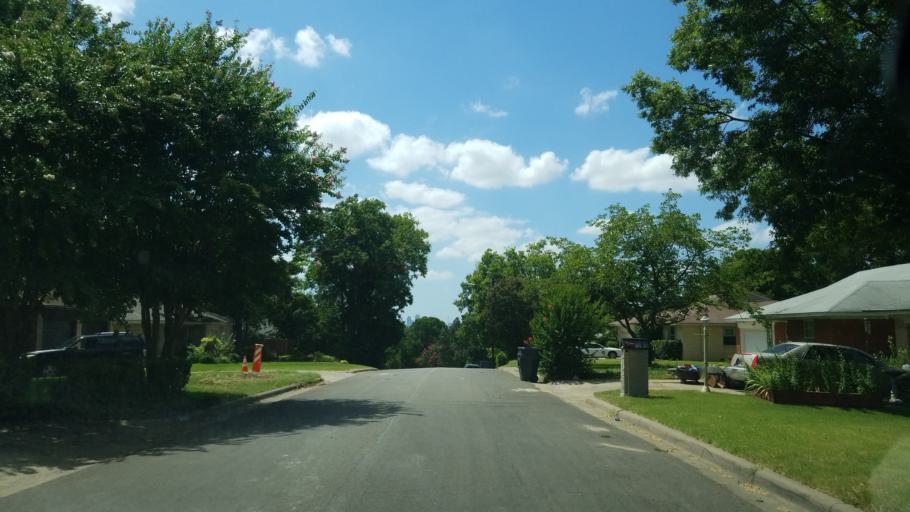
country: US
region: Texas
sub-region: Dallas County
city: Balch Springs
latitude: 32.7550
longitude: -96.6957
